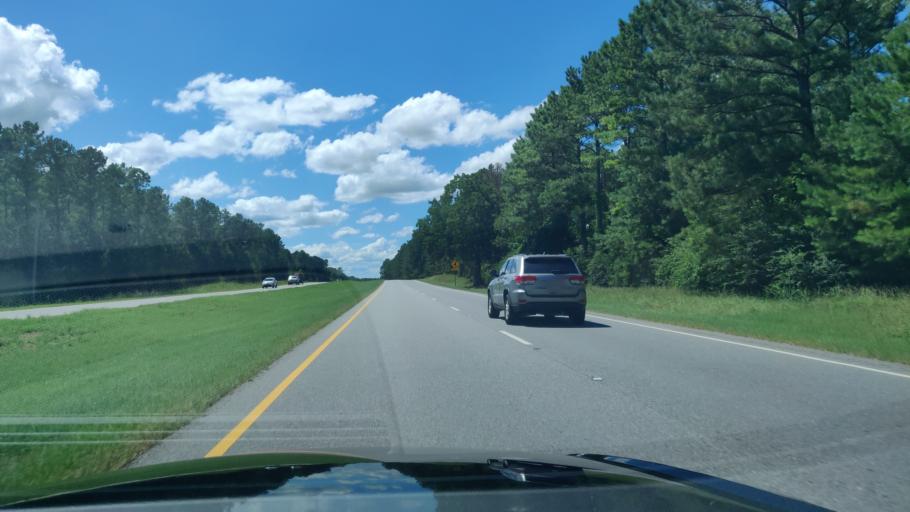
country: US
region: Georgia
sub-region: Webster County
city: Preston
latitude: 31.9155
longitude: -84.5379
